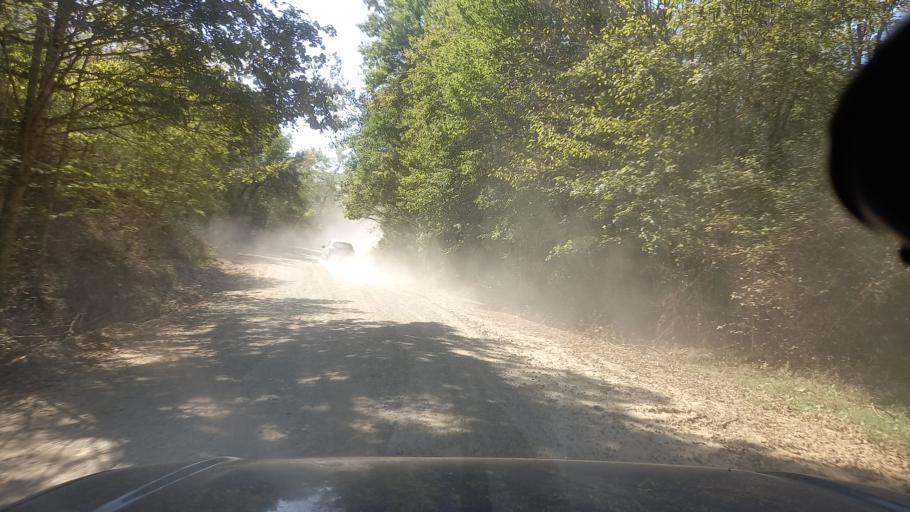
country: RU
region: Krasnodarskiy
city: Azovskaya
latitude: 44.6831
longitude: 38.6369
